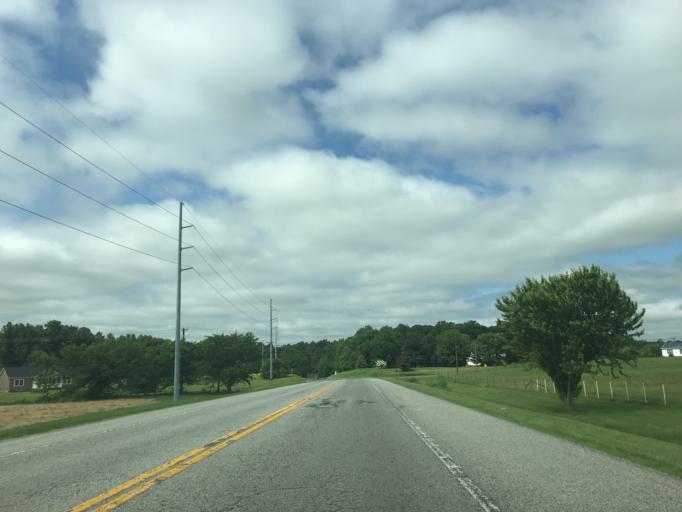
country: US
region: Maryland
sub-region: Caroline County
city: Ridgely
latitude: 38.9211
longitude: -75.9588
